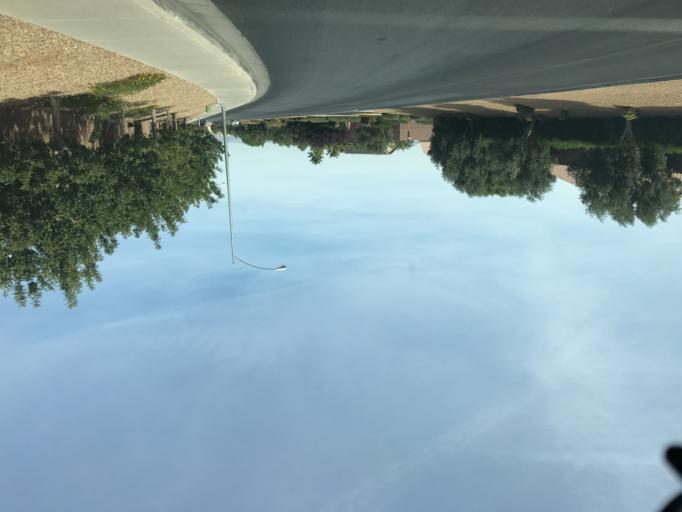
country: US
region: Nevada
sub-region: Clark County
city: Whitney
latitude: 36.1252
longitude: -115.0380
